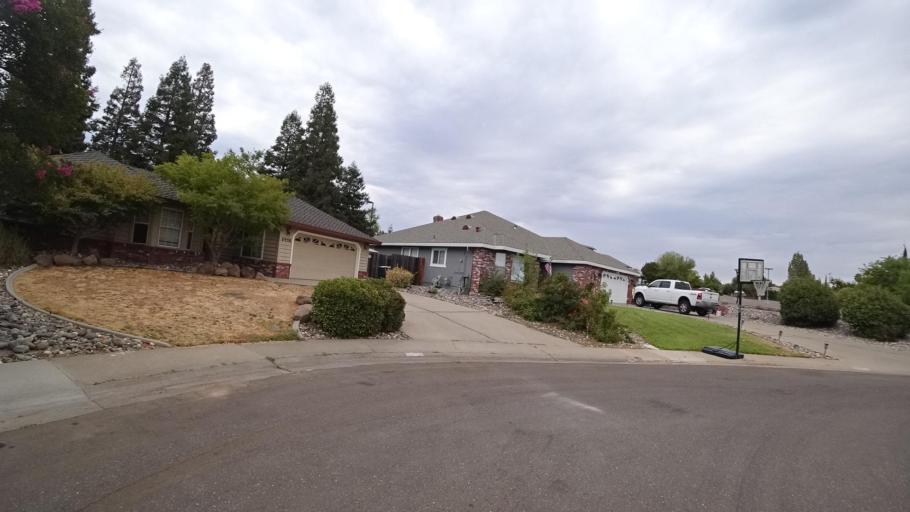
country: US
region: California
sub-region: Placer County
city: Rocklin
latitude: 38.7894
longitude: -121.2588
